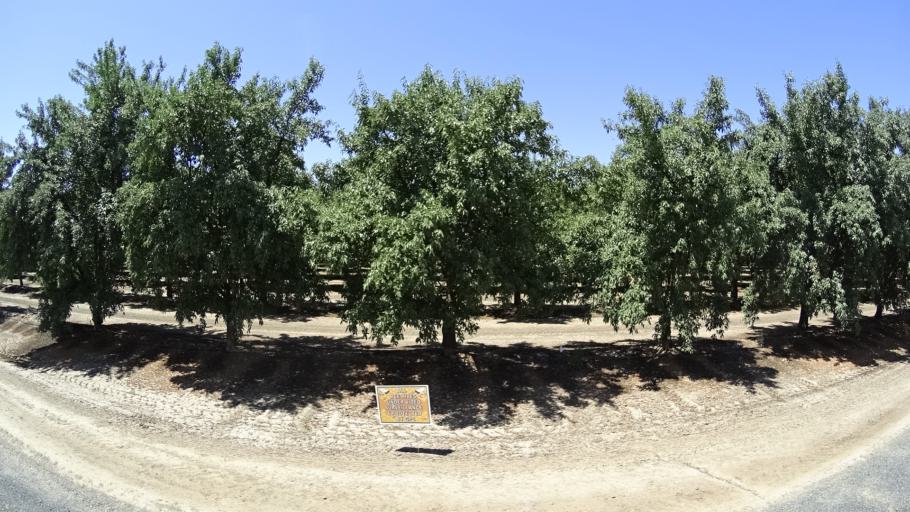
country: US
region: California
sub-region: Kings County
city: Armona
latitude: 36.3292
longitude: -119.7180
